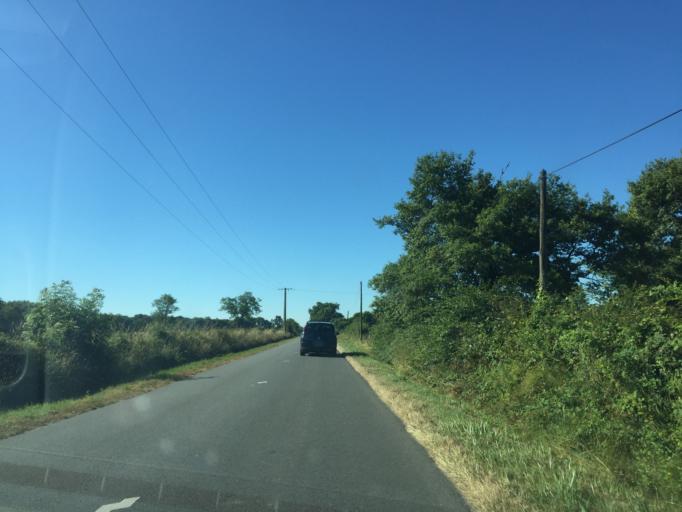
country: FR
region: Auvergne
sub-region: Departement de l'Allier
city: Dompierre-sur-Besbre
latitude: 46.5181
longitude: 3.6213
